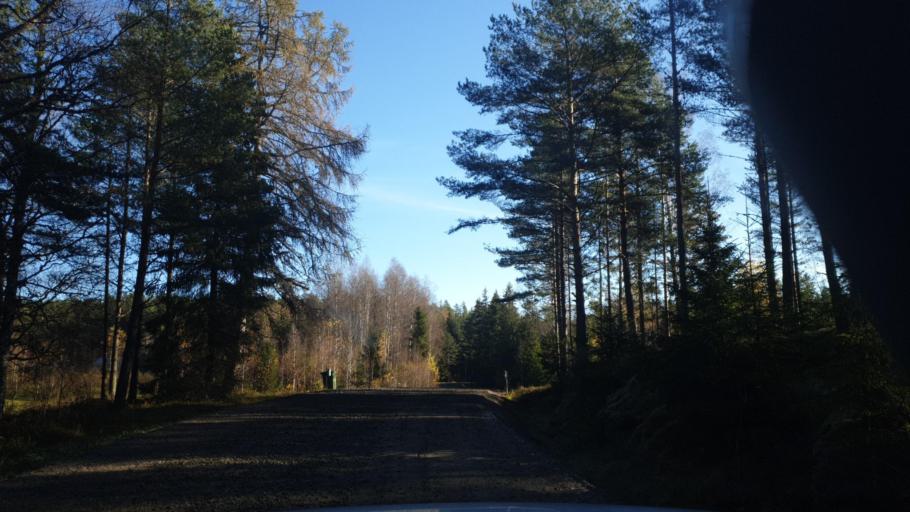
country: SE
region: Vaermland
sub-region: Karlstads Kommun
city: Valberg
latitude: 59.4165
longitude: 13.1477
